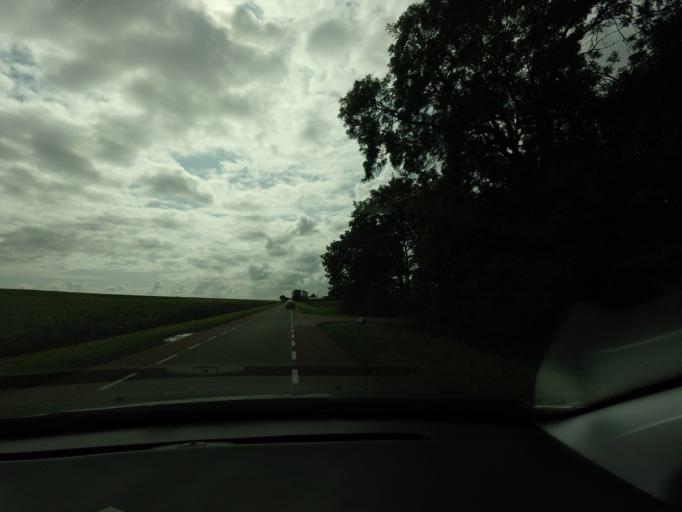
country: NL
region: North Holland
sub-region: Gemeente Medemblik
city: Medemblik
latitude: 52.8350
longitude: 5.1111
